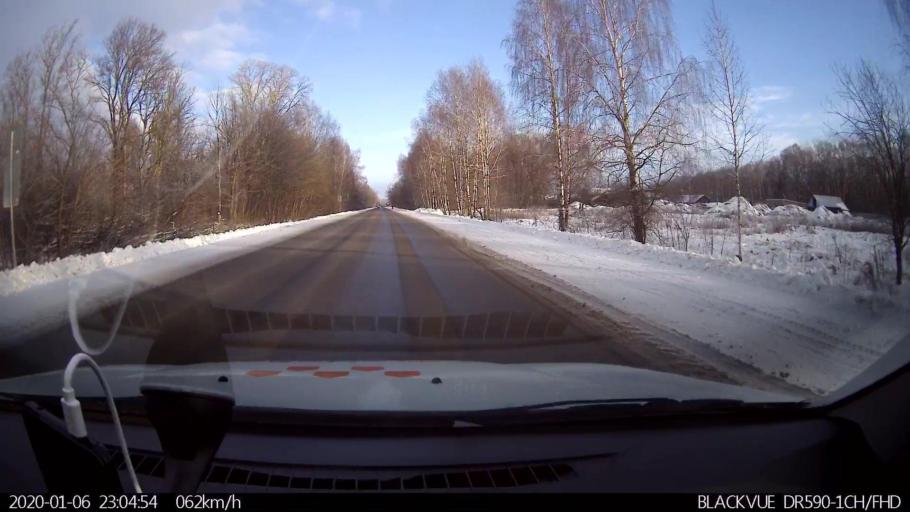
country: RU
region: Nizjnij Novgorod
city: Bogorodsk
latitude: 56.1185
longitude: 43.5475
